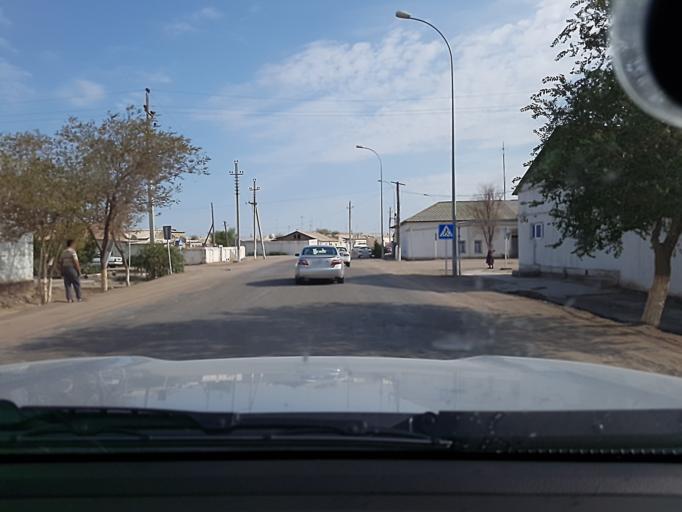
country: TM
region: Dasoguz
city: Koeneuergench
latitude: 42.3245
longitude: 59.1599
